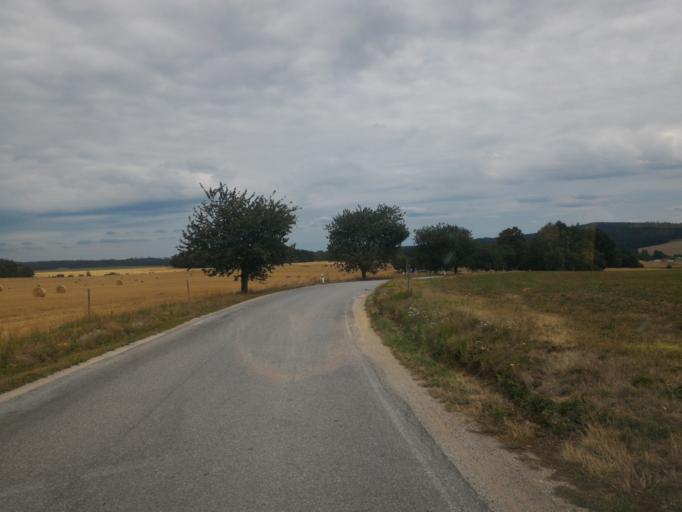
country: CZ
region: Jihocesky
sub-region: Okres Jindrichuv Hradec
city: Dacice
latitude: 49.0909
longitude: 15.4620
